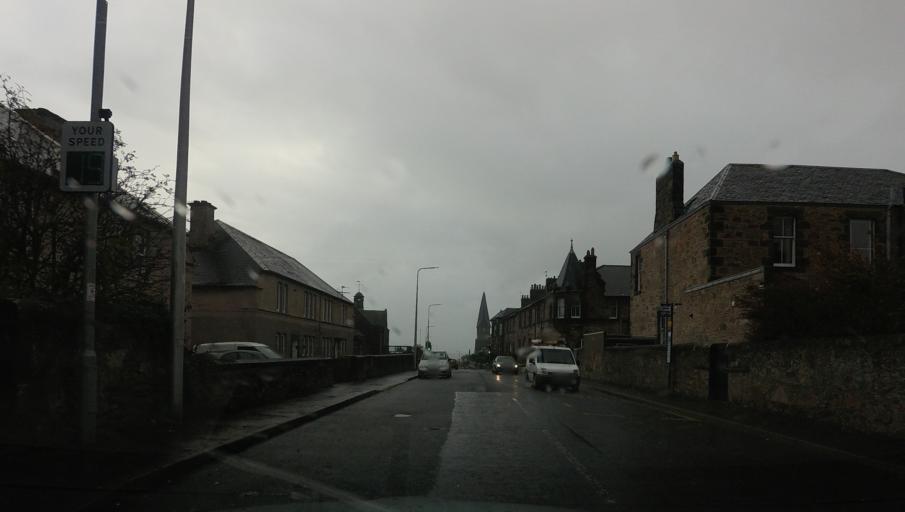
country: GB
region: Scotland
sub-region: Fife
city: Kirkcaldy
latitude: 56.1300
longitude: -3.1217
